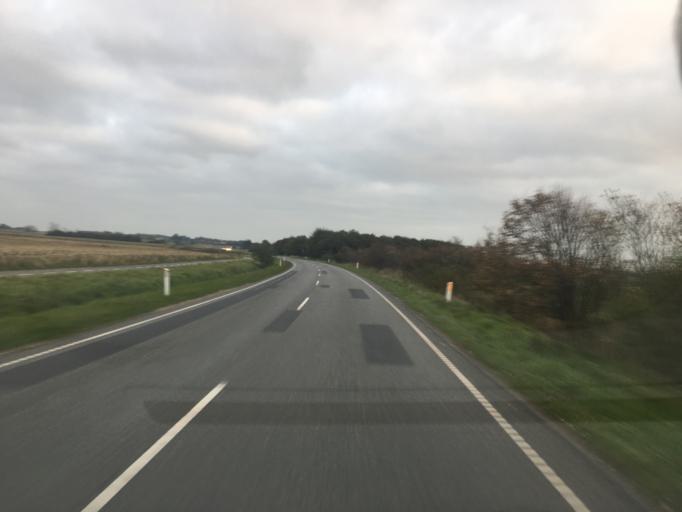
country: DE
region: Schleswig-Holstein
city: Aventoft
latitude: 54.9552
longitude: 8.7700
